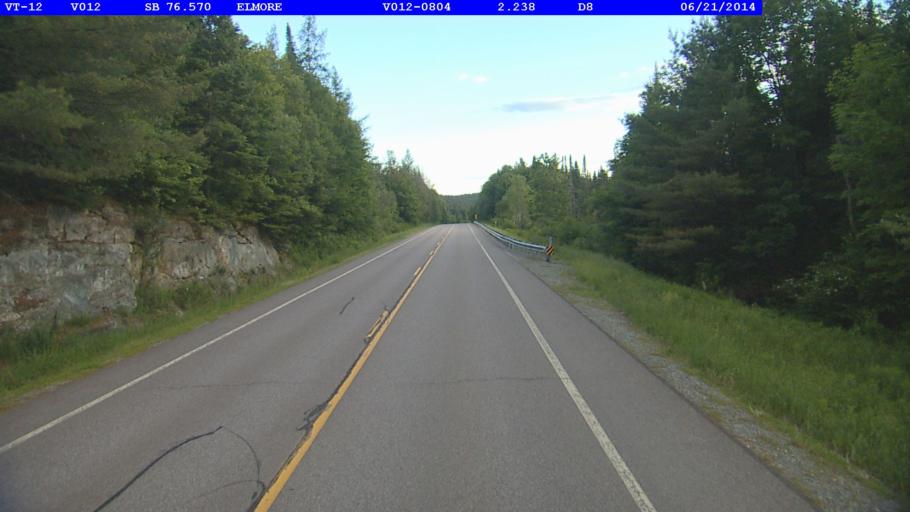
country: US
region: Vermont
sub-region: Lamoille County
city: Morrisville
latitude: 44.4792
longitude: -72.5288
